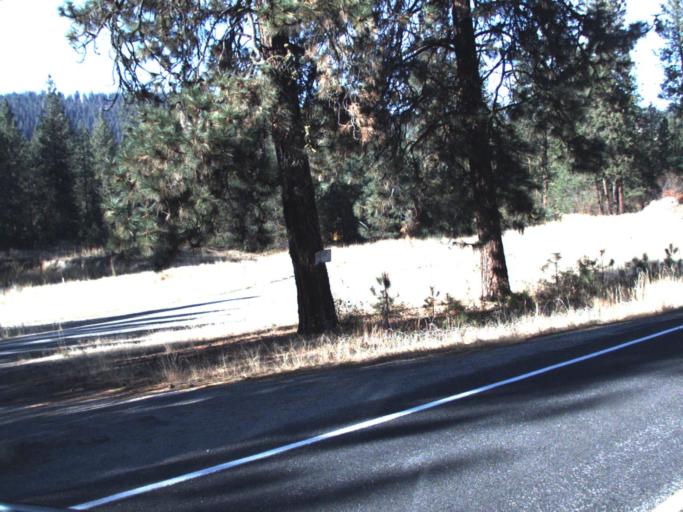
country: US
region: Washington
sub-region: Stevens County
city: Kettle Falls
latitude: 48.2110
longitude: -118.1783
